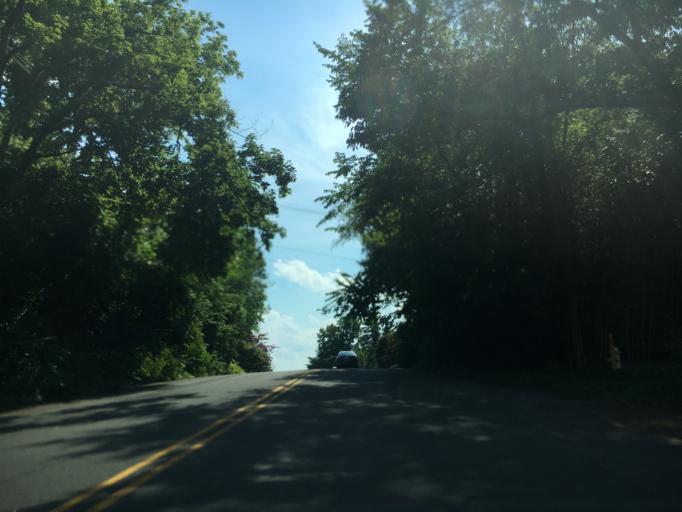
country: US
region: Pennsylvania
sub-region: Berks County
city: Wyomissing
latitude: 40.3221
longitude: -75.9577
